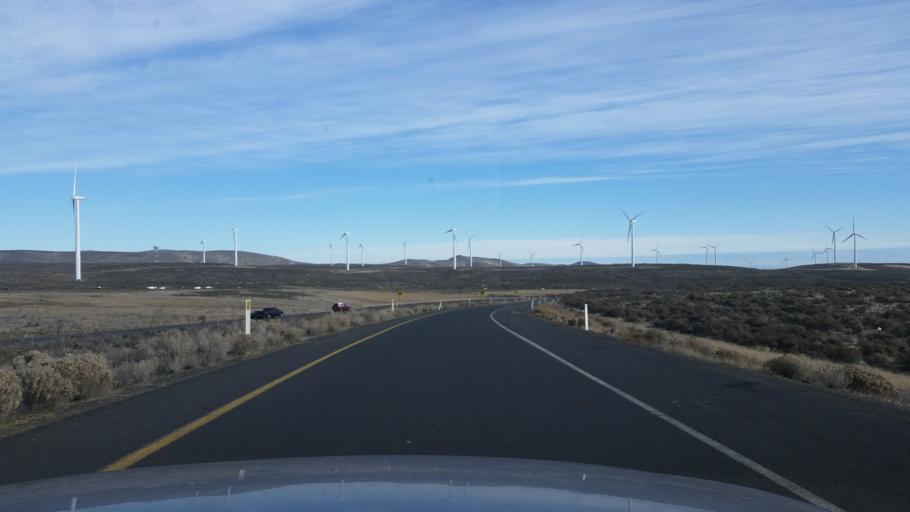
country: US
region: Washington
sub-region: Kittitas County
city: Kittitas
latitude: 46.9420
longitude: -120.2027
